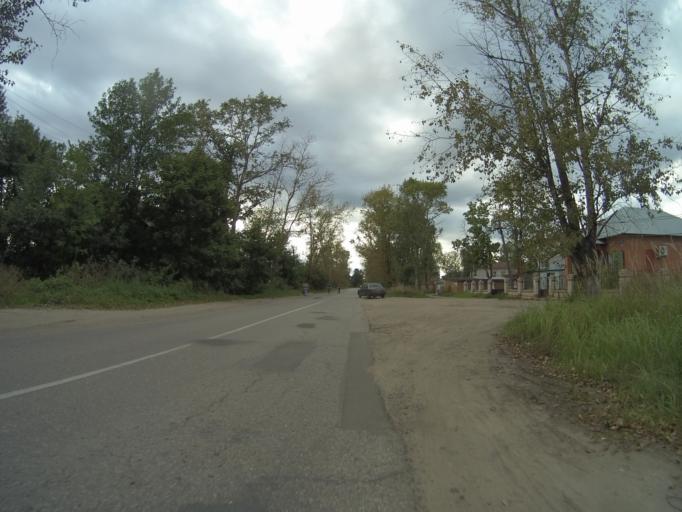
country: RU
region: Vladimir
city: Golovino
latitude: 55.9508
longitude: 40.4389
